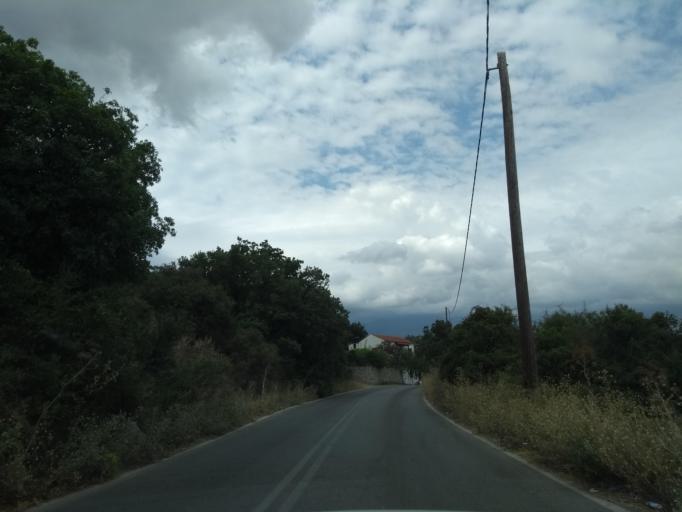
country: GR
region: Crete
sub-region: Nomos Chanias
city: Kalivai
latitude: 35.4085
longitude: 24.2066
